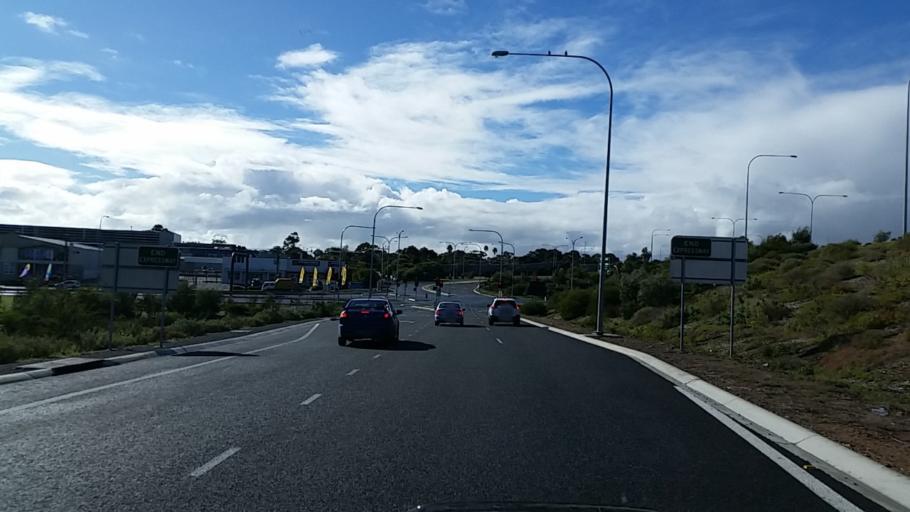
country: AU
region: South Australia
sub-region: Onkaparinga
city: Reynella
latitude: -35.1072
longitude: 138.5090
